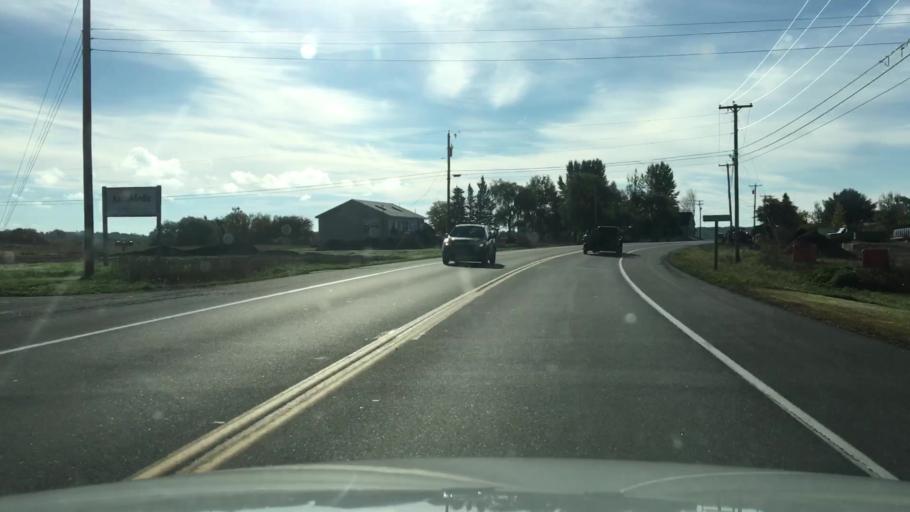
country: US
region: Maine
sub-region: Knox County
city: Warren
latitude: 44.0833
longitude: -69.2272
